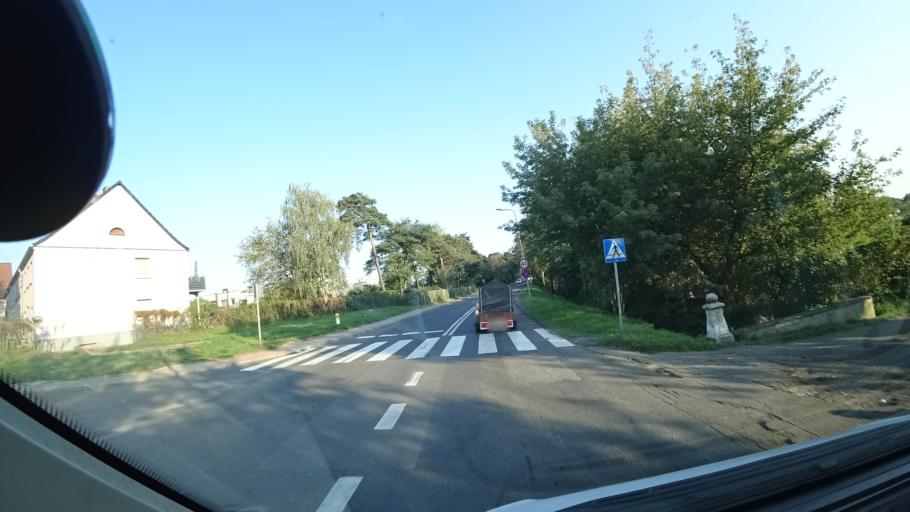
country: PL
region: Opole Voivodeship
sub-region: Powiat kedzierzynsko-kozielski
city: Kedzierzyn-Kozle
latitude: 50.3351
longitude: 18.1915
